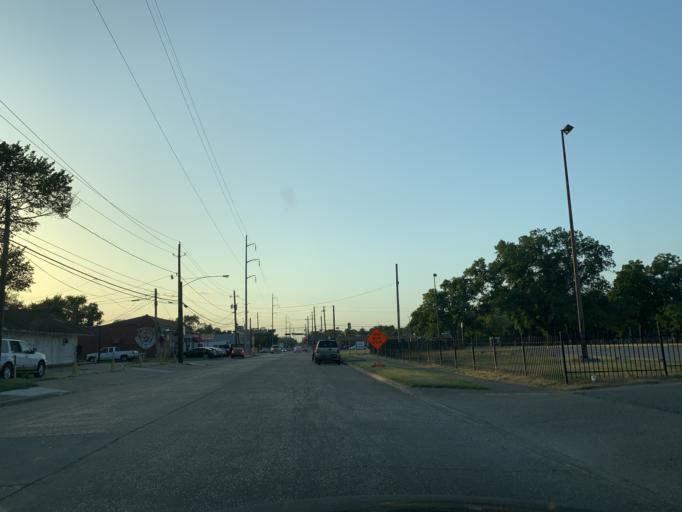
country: US
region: Texas
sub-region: Dallas County
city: Dallas
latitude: 32.7551
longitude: -96.7517
